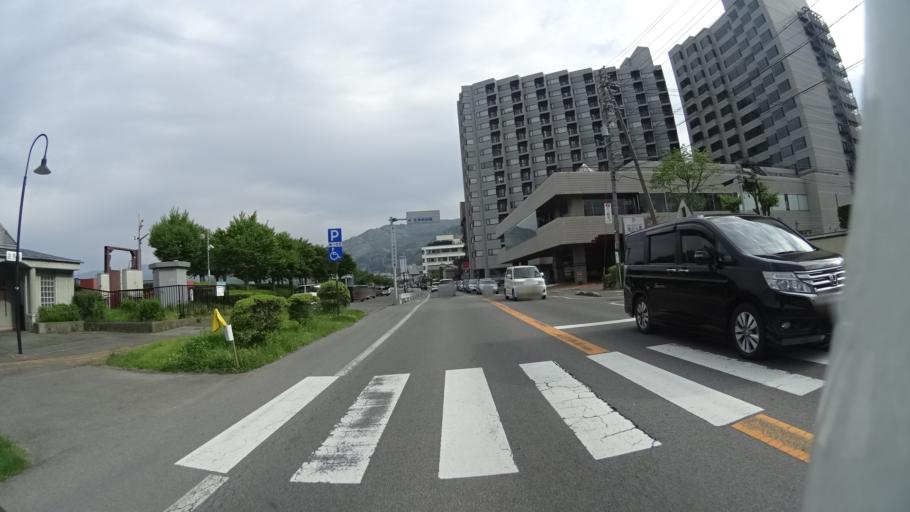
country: JP
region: Nagano
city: Suwa
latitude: 36.0508
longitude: 138.1129
